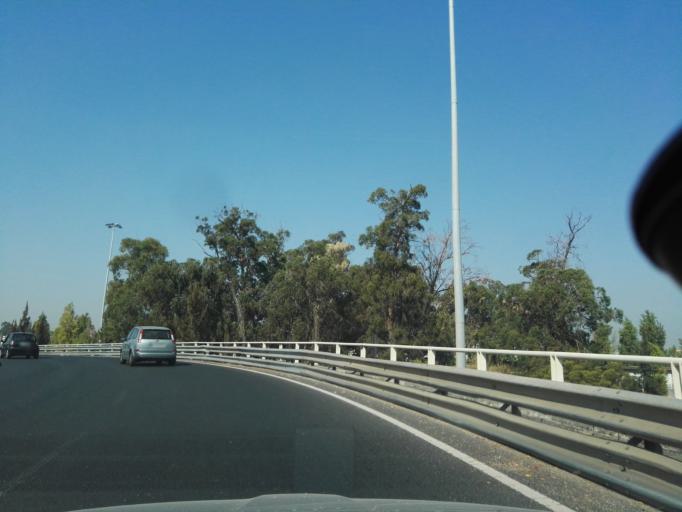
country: PT
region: Lisbon
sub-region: Loures
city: Sacavem
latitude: 38.7815
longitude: -9.1227
